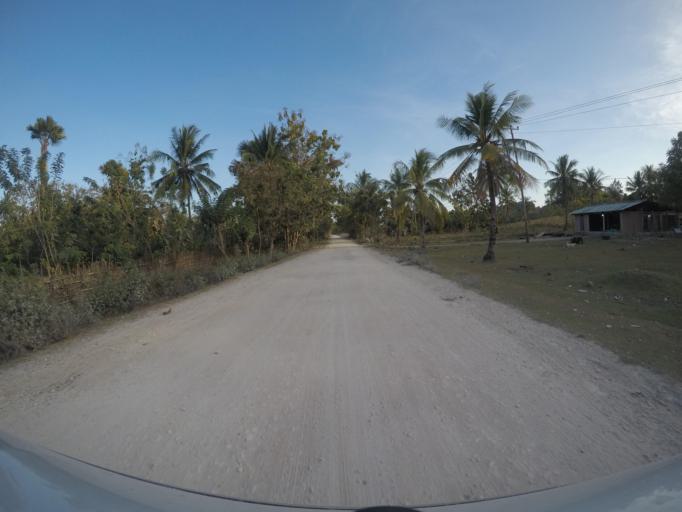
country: TL
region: Viqueque
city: Viqueque
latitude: -8.8762
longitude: 126.5077
